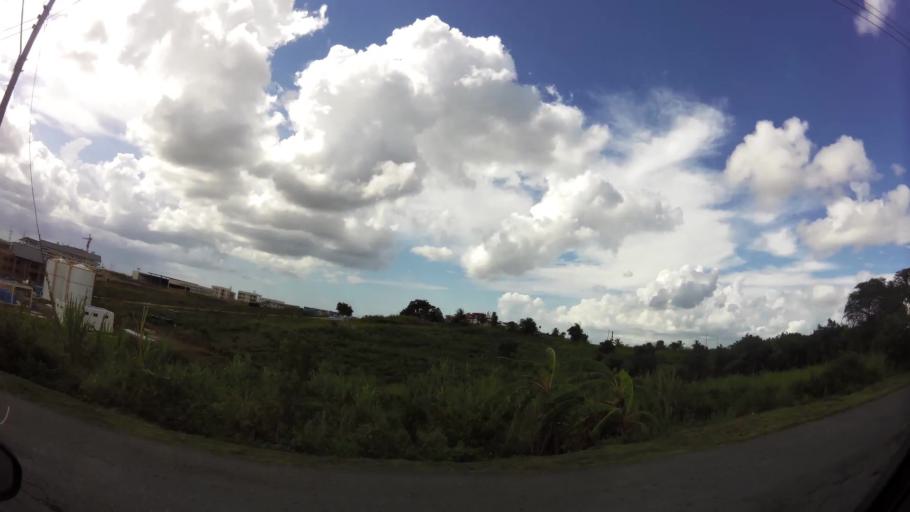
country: TT
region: Penal/Debe
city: Debe
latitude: 10.2233
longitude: -61.4420
